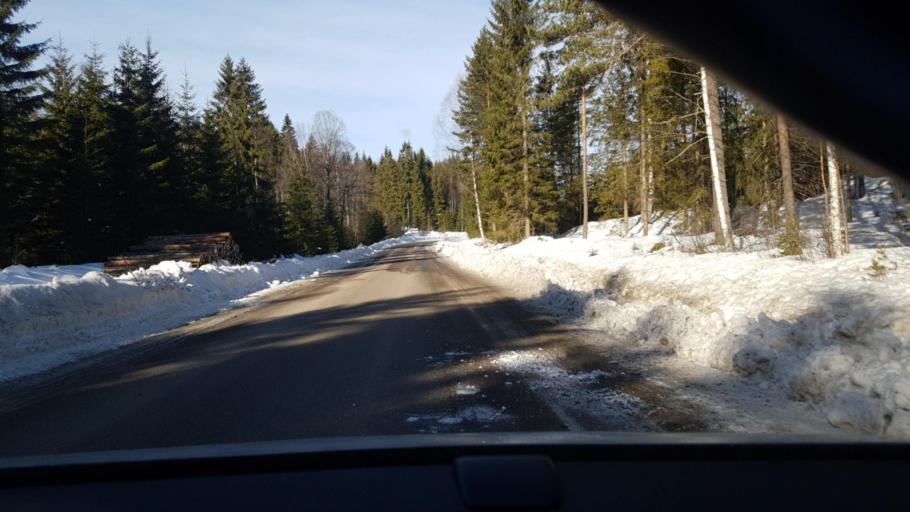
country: NO
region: Hedmark
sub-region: Eidskog
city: Skotterud
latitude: 59.8052
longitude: 12.1284
